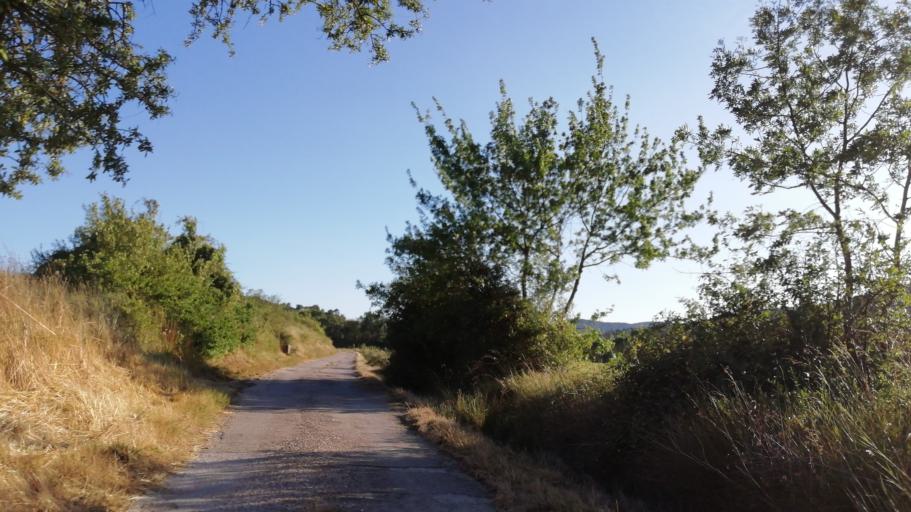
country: FR
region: Languedoc-Roussillon
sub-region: Departement de l'Herault
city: Saint-Martin-de-Londres
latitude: 43.7810
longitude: 3.7284
